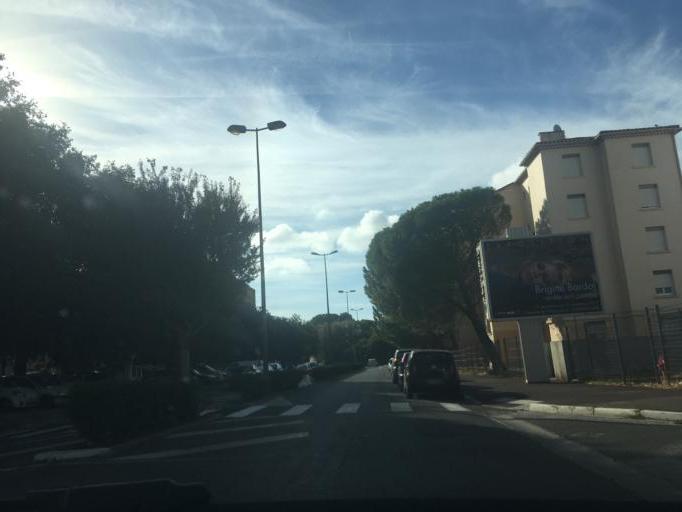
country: FR
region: Provence-Alpes-Cote d'Azur
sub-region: Departement du Var
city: Draguignan
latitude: 43.5394
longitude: 6.4578
